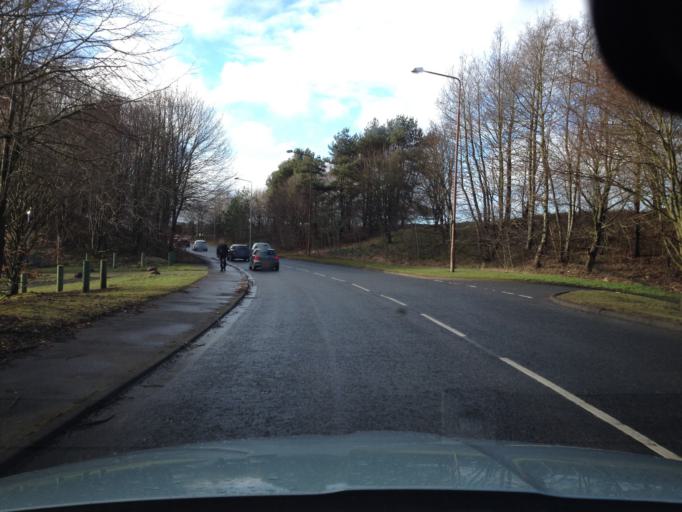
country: GB
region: Scotland
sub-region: West Lothian
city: Livingston
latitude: 55.8819
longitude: -3.5409
